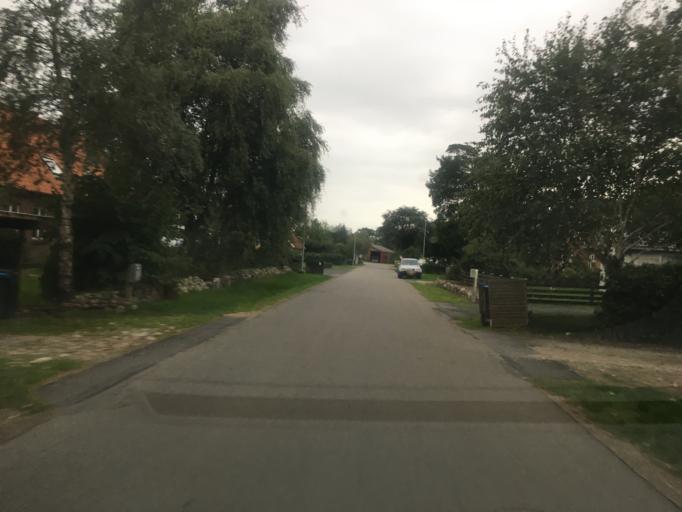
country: DE
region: Schleswig-Holstein
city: Ellhoft
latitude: 54.9479
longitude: 8.9681
